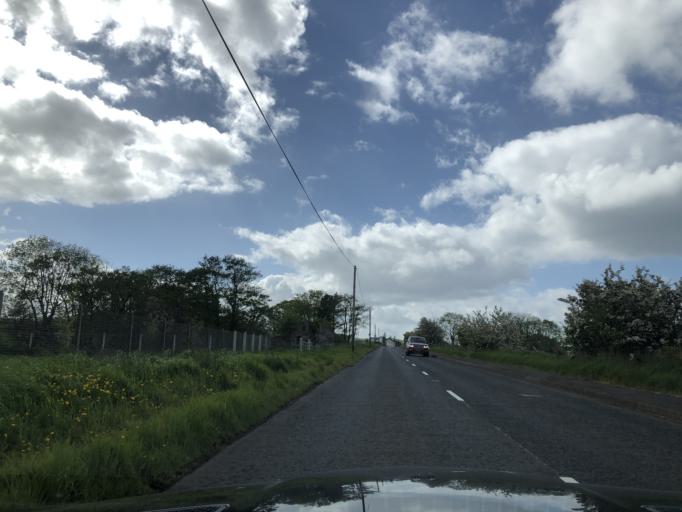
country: GB
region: Northern Ireland
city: Bushmills
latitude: 55.2067
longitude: -6.5344
